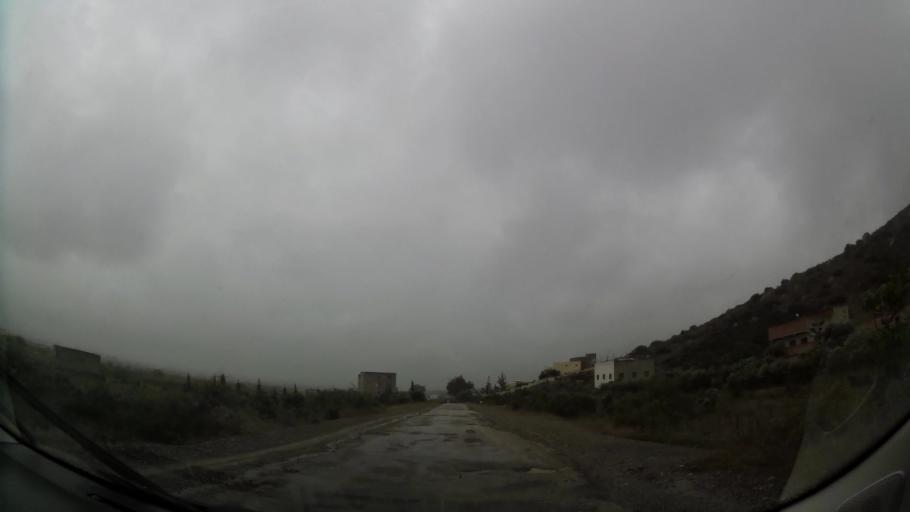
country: MA
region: Taza-Al Hoceima-Taounate
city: Imzourene
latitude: 35.1300
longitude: -3.7802
